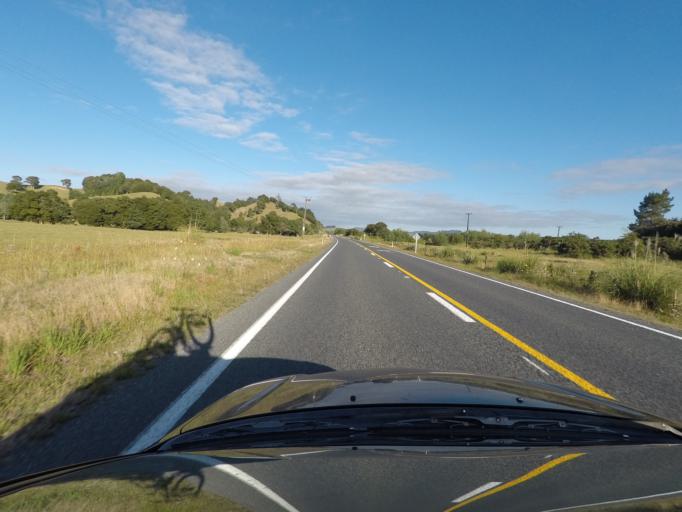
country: NZ
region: Northland
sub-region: Whangarei
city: Maungatapere
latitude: -35.5338
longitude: 174.2305
